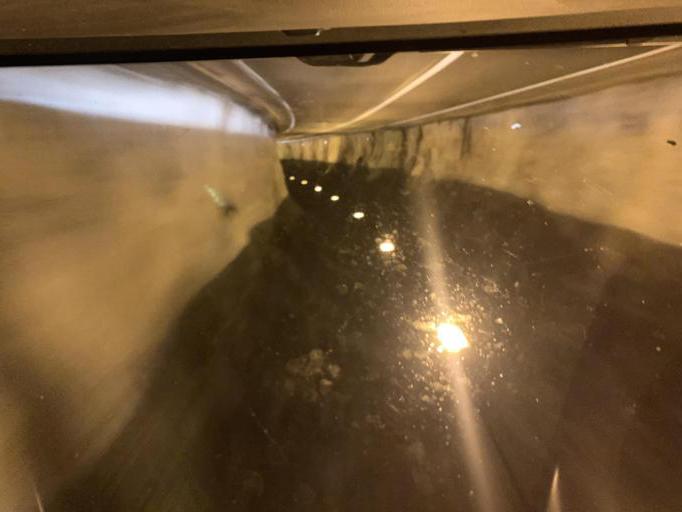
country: IT
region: Trentino-Alto Adige
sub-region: Bolzano
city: Avelengo
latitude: 46.6466
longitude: 11.2085
